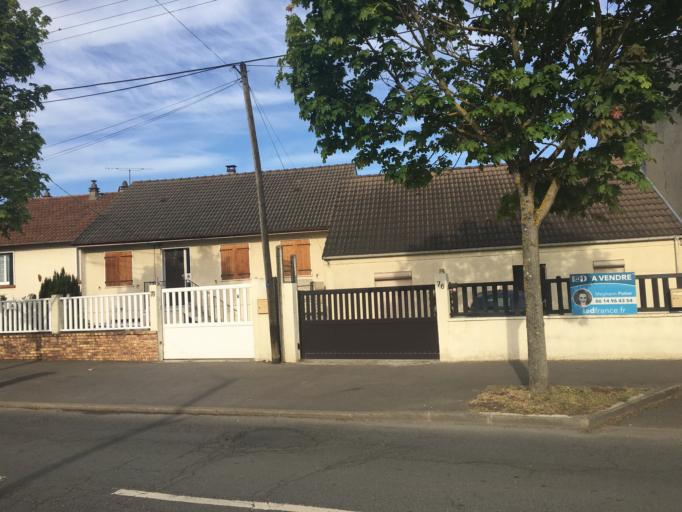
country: FR
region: Ile-de-France
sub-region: Departement de l'Essonne
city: Fleury-Merogis
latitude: 48.6528
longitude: 2.3692
